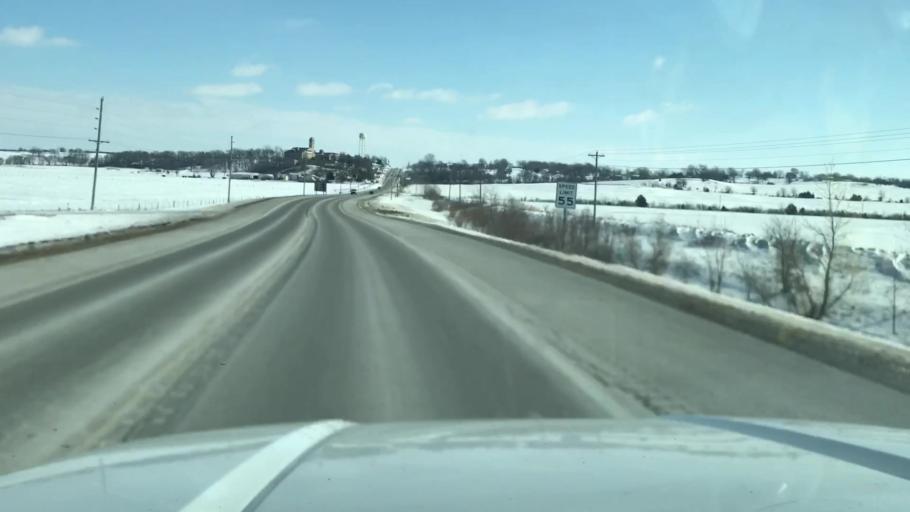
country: US
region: Missouri
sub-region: Nodaway County
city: Maryville
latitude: 40.3449
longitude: -94.8291
